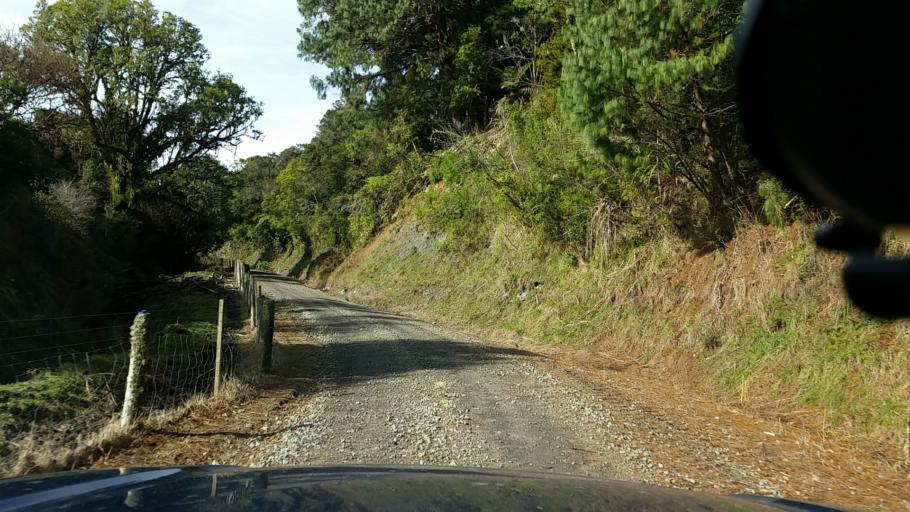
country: NZ
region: Taranaki
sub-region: New Plymouth District
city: Waitara
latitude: -39.0345
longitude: 174.7800
